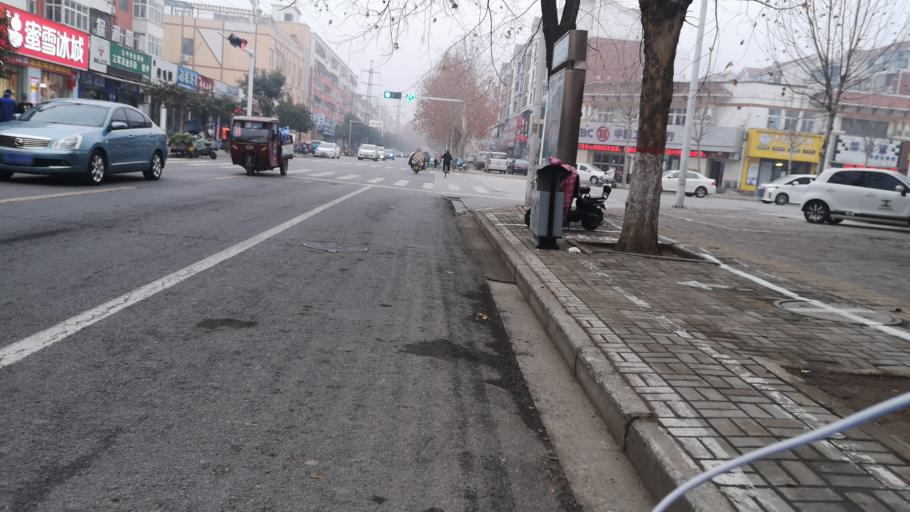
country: CN
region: Henan Sheng
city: Zhongyuanlu
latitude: 35.7647
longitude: 115.0745
